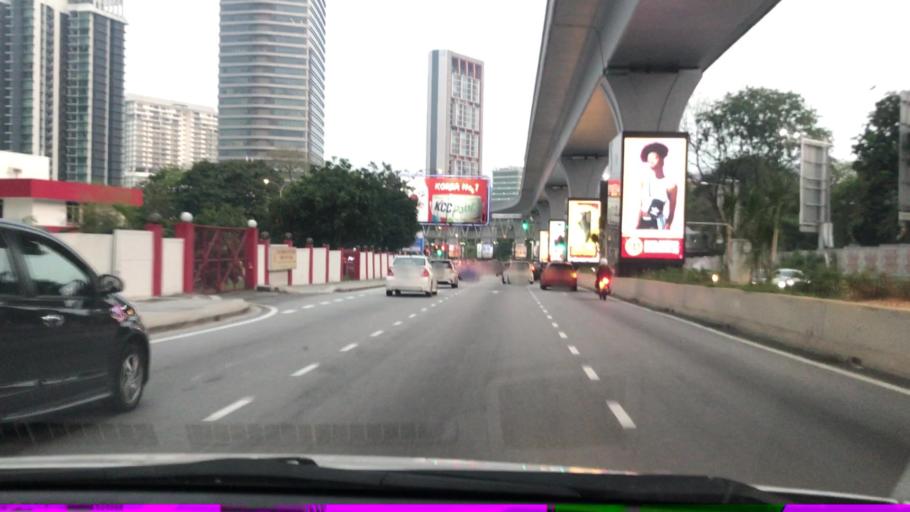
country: MY
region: Selangor
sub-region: Petaling
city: Petaling Jaya
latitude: 3.1401
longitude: 101.6270
